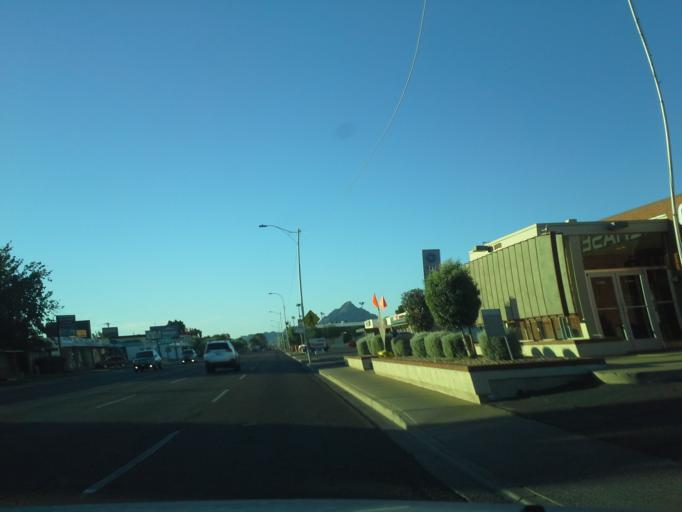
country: US
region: Arizona
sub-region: Maricopa County
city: Phoenix
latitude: 33.4823
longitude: -112.0301
